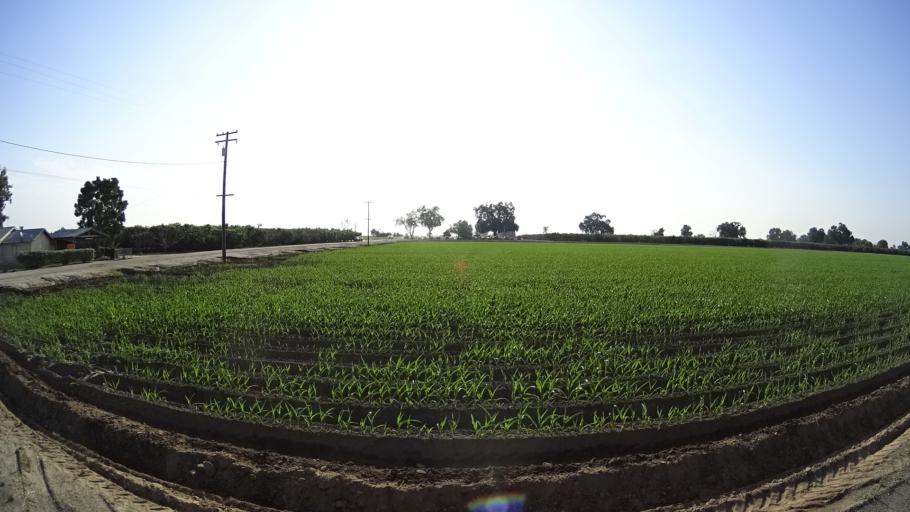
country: US
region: California
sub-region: Kings County
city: Lemoore
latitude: 36.3798
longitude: -119.7936
